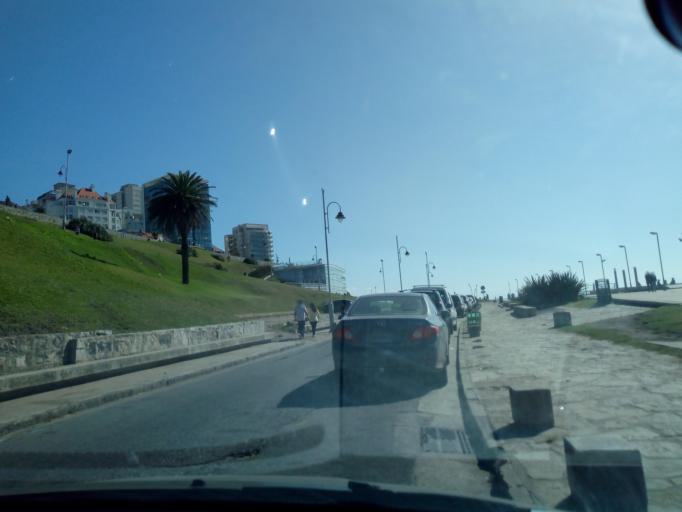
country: AR
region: Buenos Aires
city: Mar del Plata
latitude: -38.0138
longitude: -57.5315
